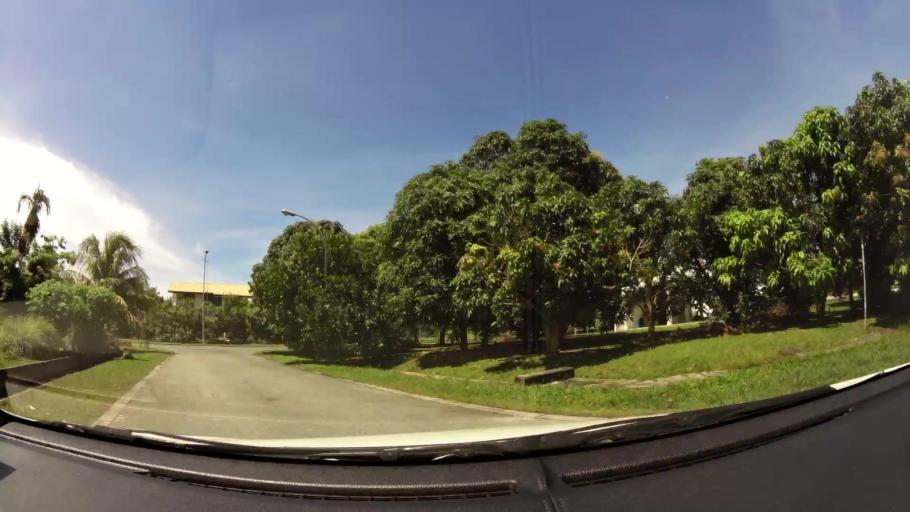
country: BN
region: Belait
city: Kuala Belait
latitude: 4.5858
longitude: 114.2271
